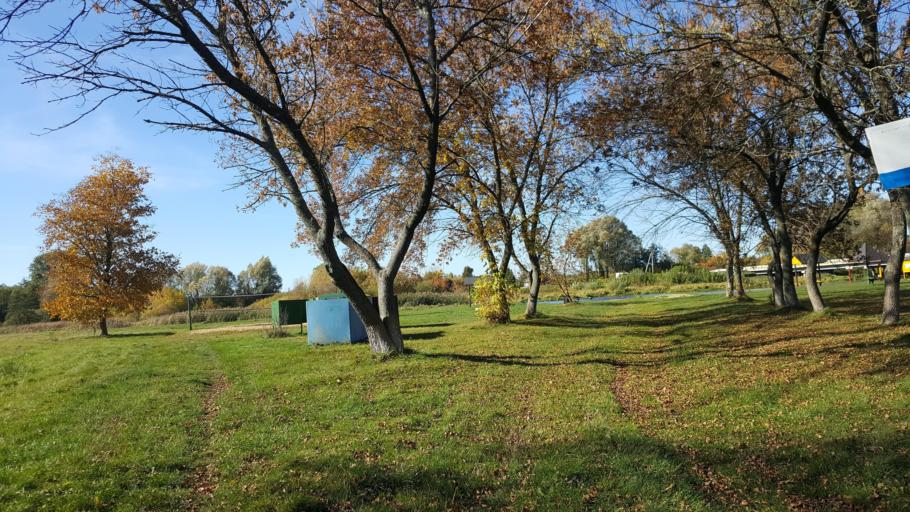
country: BY
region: Brest
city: Kamyanyets
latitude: 52.4007
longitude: 23.8040
